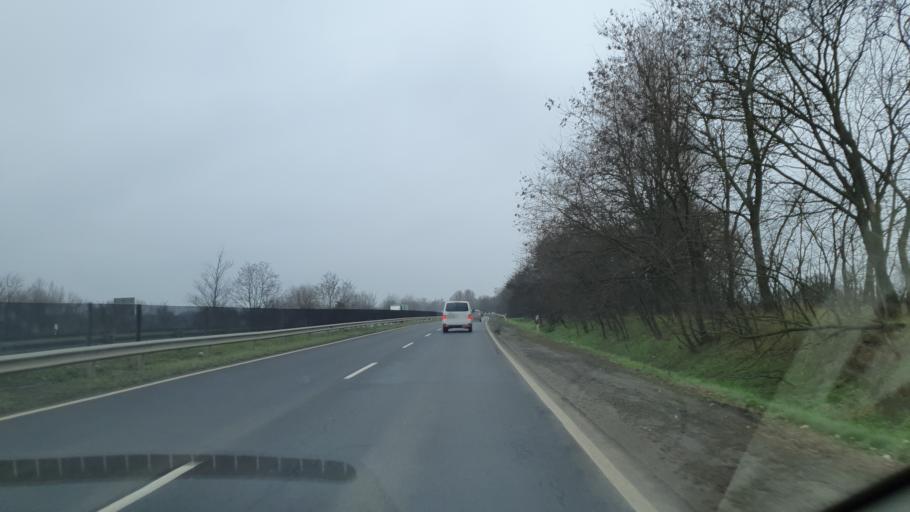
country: HU
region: Szabolcs-Szatmar-Bereg
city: Nyiregyhaza
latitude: 47.8970
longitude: 21.7105
